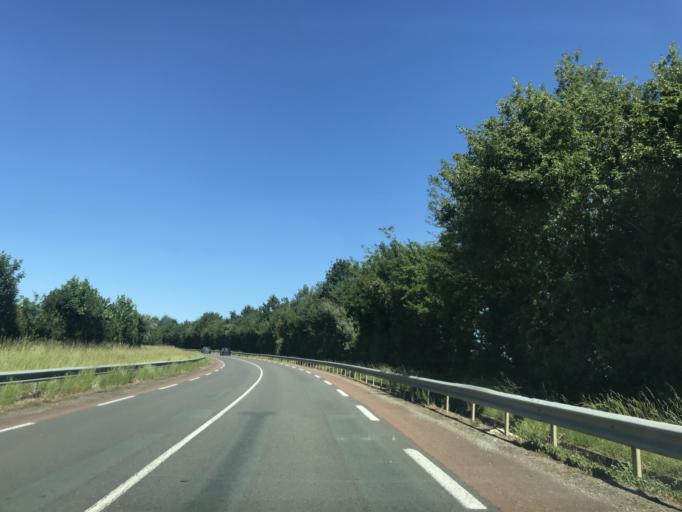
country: FR
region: Poitou-Charentes
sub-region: Departement de la Charente-Maritime
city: Gemozac
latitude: 45.5731
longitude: -0.6580
